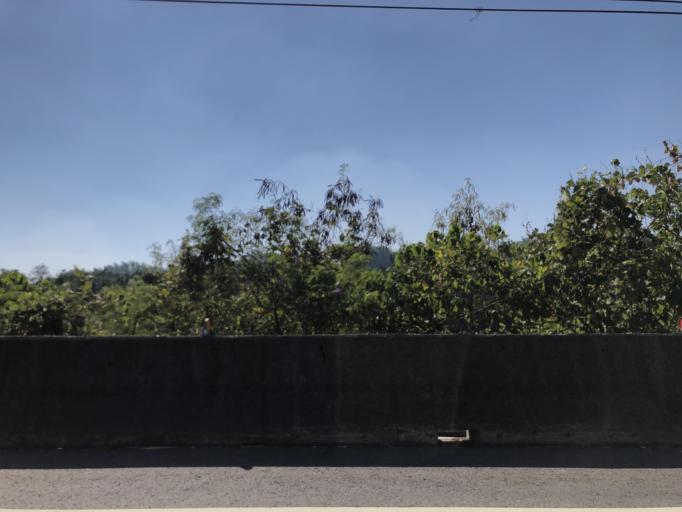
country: TW
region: Taiwan
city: Yujing
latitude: 23.0594
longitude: 120.3943
